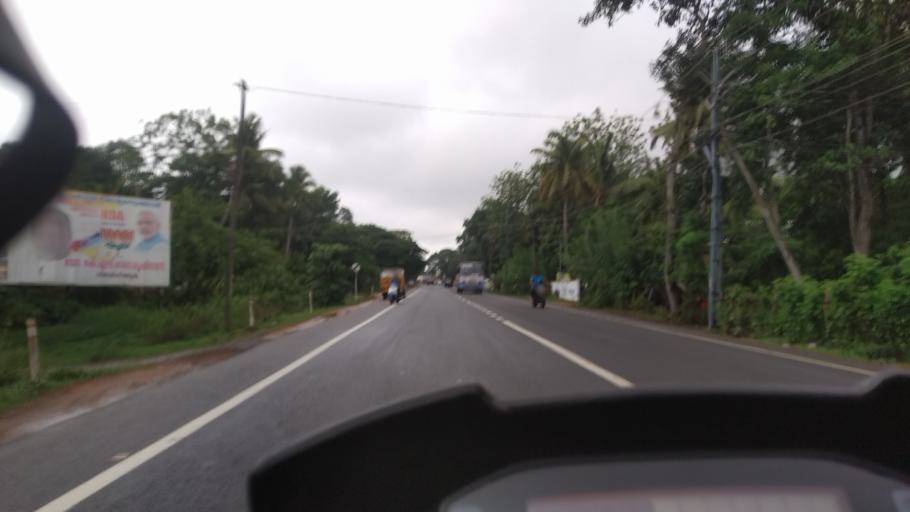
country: IN
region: Kerala
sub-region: Alappuzha
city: Mavelikara
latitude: 9.3186
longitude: 76.4226
